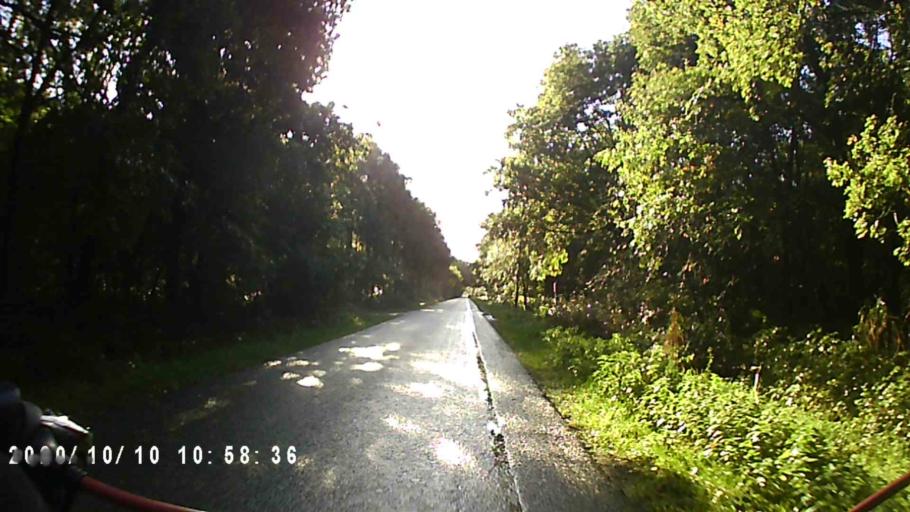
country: NL
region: Friesland
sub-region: Gemeente Achtkarspelen
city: Surhuisterveen
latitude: 53.1445
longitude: 6.2071
